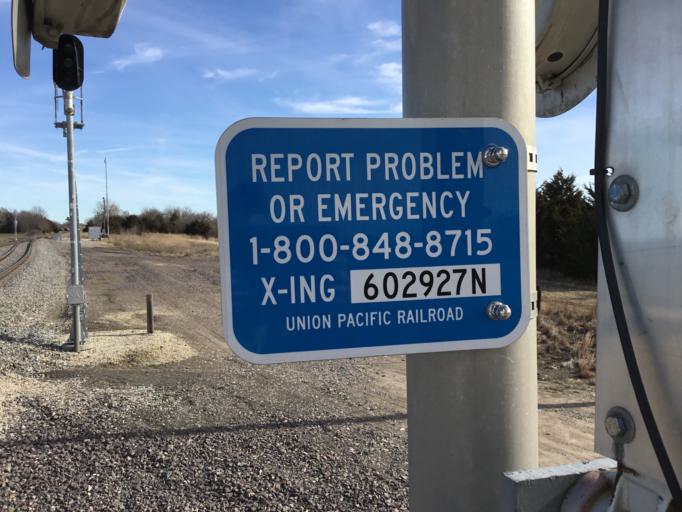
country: US
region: Kansas
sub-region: McPherson County
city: McPherson
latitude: 38.3844
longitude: -97.4820
